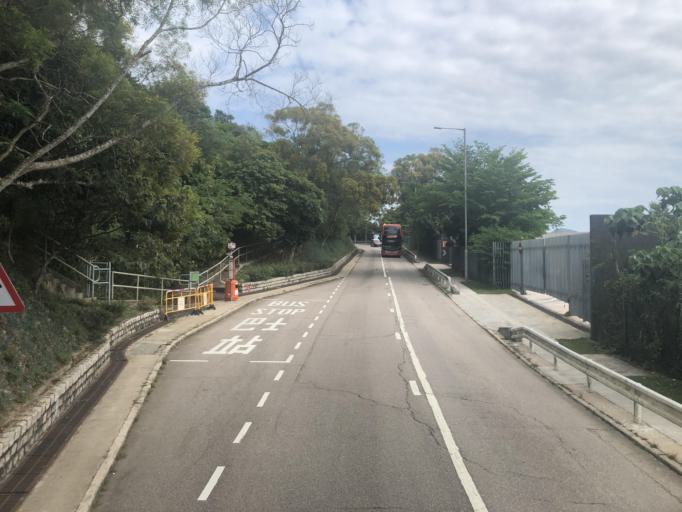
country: HK
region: Sai Kung
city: Sai Kung
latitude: 22.3879
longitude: 114.3029
